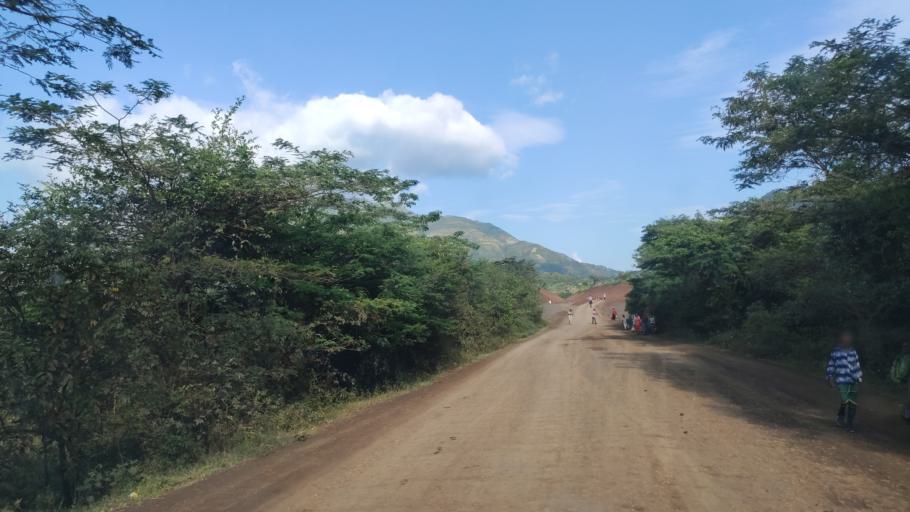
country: ET
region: Southern Nations, Nationalities, and People's Region
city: Felege Neway
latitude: 6.4264
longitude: 37.3194
